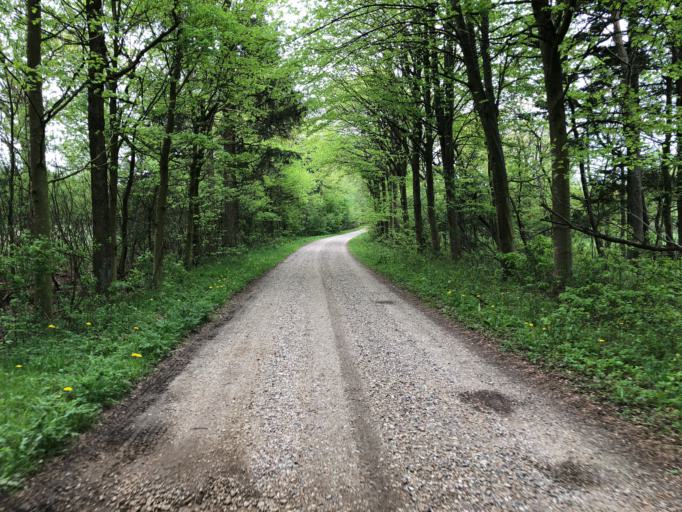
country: DK
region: Central Jutland
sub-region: Holstebro Kommune
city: Ulfborg
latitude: 56.2697
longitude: 8.4280
